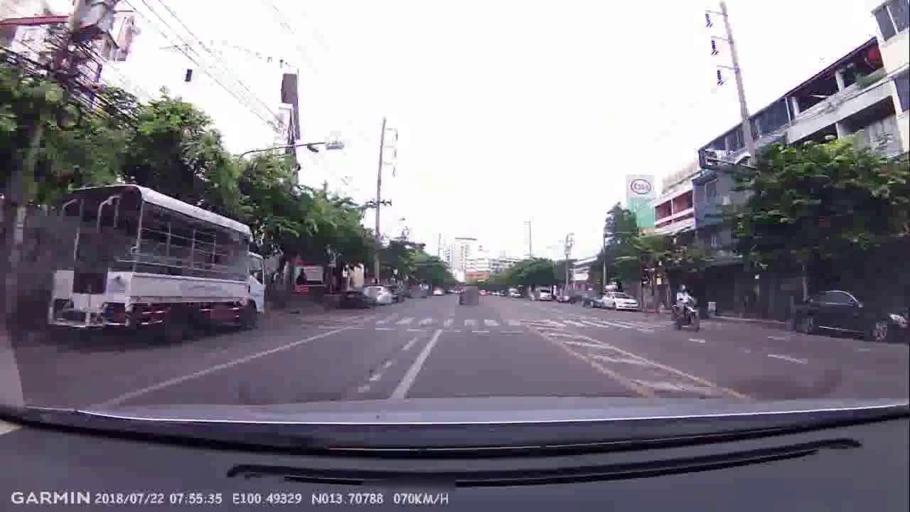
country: TH
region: Bangkok
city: Bang Kho Laem
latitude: 13.7078
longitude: 100.4931
